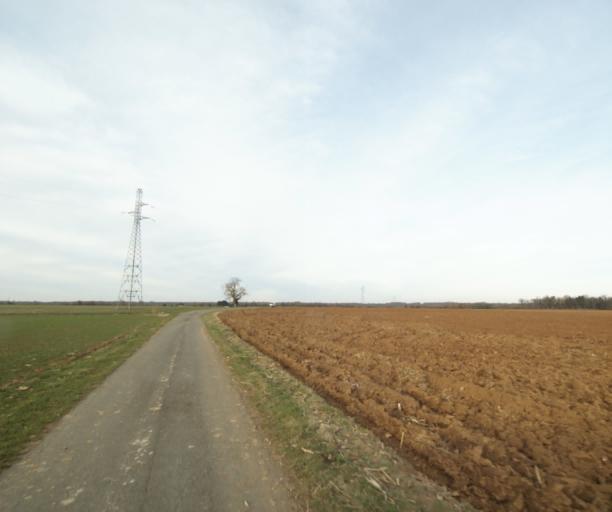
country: FR
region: Poitou-Charentes
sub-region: Departement de la Charente-Maritime
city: Saint-Hilaire-de-Villefranche
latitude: 45.8296
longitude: -0.5809
